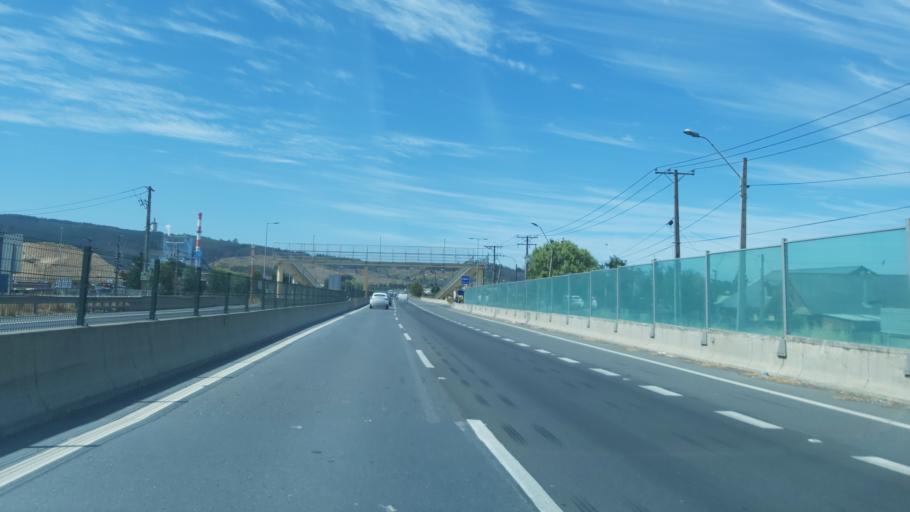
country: CL
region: Biobio
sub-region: Provincia de Concepcion
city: Coronel
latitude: -37.0314
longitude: -73.1349
